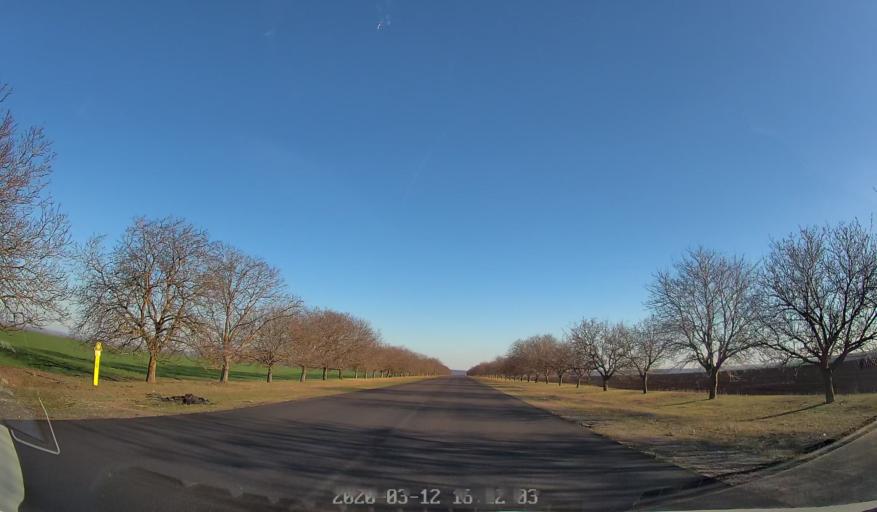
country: MD
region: Anenii Noi
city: Anenii Noi
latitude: 46.9405
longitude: 29.2674
